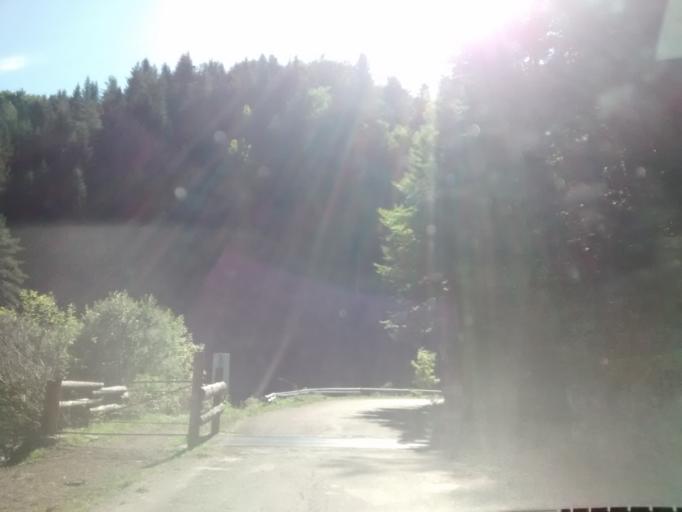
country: ES
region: Aragon
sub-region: Provincia de Huesca
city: Aragues del Puerto
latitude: 42.8300
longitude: -0.7118
